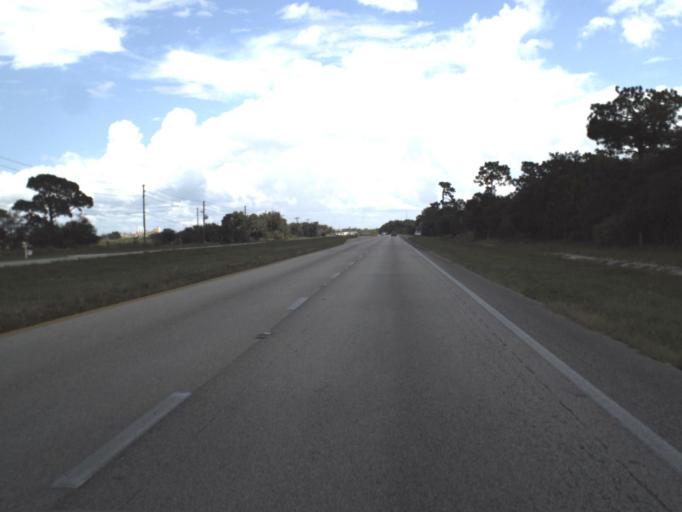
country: US
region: Florida
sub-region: Polk County
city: Babson Park
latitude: 27.8939
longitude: -81.5220
